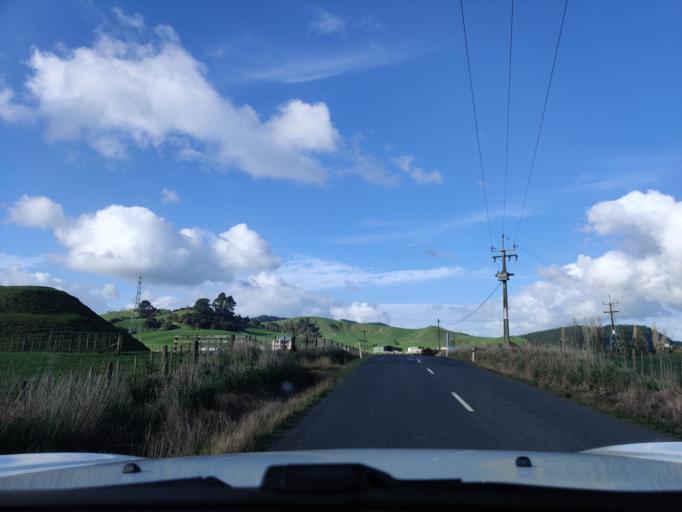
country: NZ
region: Waikato
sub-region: Waikato District
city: Te Kauwhata
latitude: -37.2857
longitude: 175.2133
